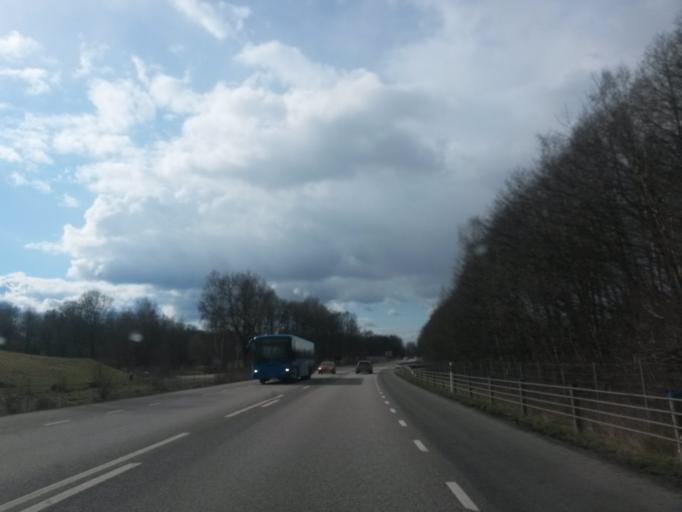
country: SE
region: Vaestra Goetaland
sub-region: Skara Kommun
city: Axvall
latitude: 58.3801
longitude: 13.6862
